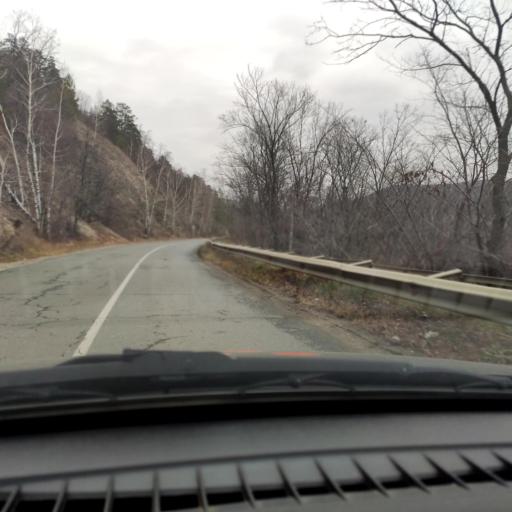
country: RU
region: Samara
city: Povolzhskiy
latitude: 53.4358
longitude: 49.6691
